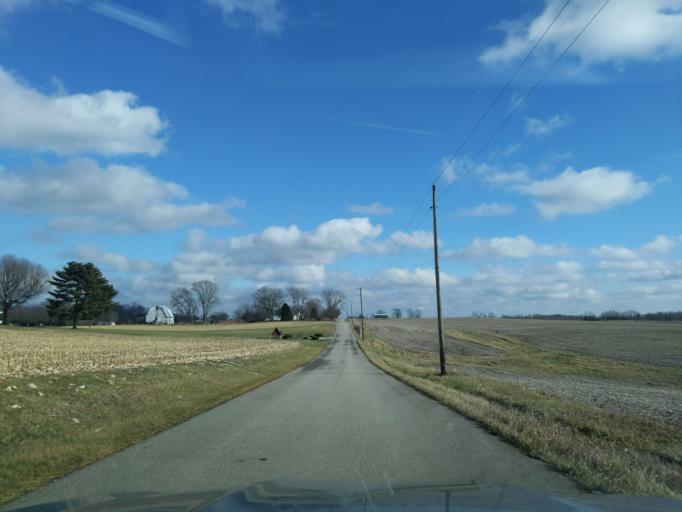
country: US
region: Indiana
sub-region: Decatur County
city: Greensburg
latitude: 39.2781
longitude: -85.4766
